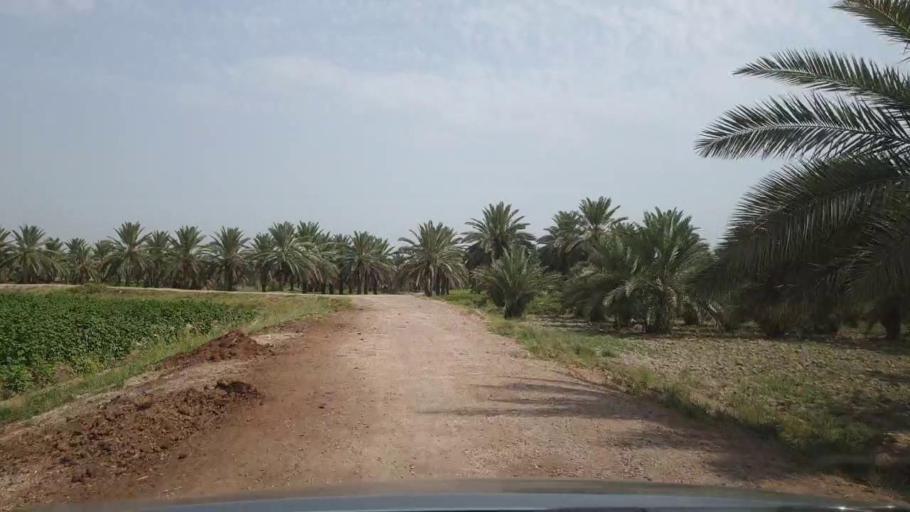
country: PK
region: Sindh
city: Rohri
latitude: 27.6847
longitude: 69.0364
